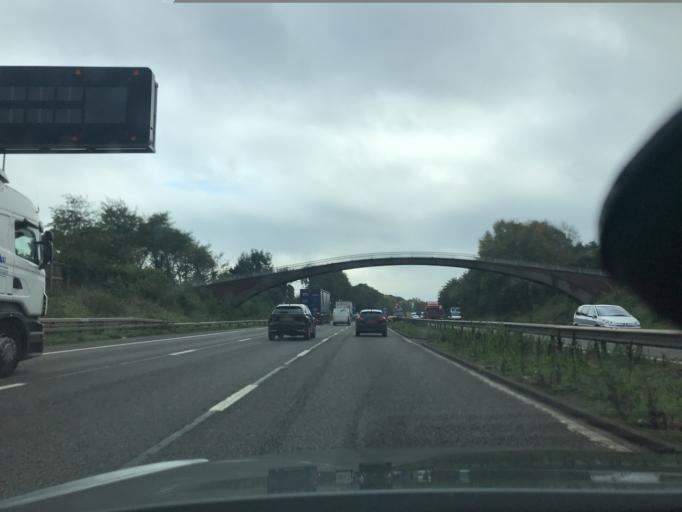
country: GB
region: England
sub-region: Staffordshire
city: Stafford
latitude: 52.7814
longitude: -2.1224
